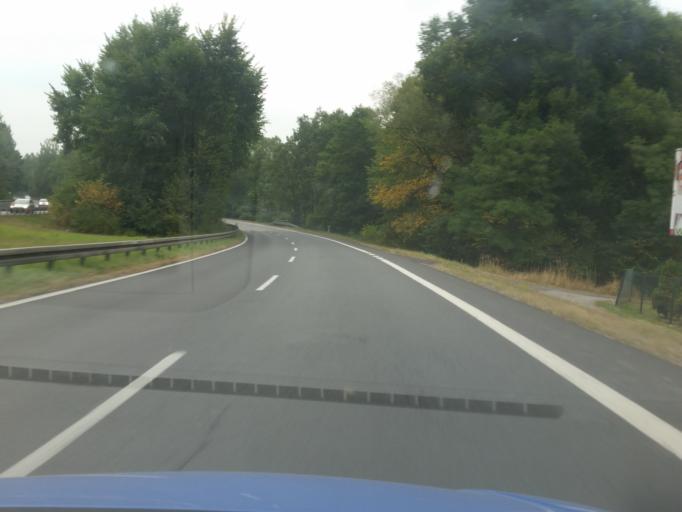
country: PL
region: Silesian Voivodeship
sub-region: Powiat bedzinski
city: Sarnow
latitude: 50.3854
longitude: 19.1809
